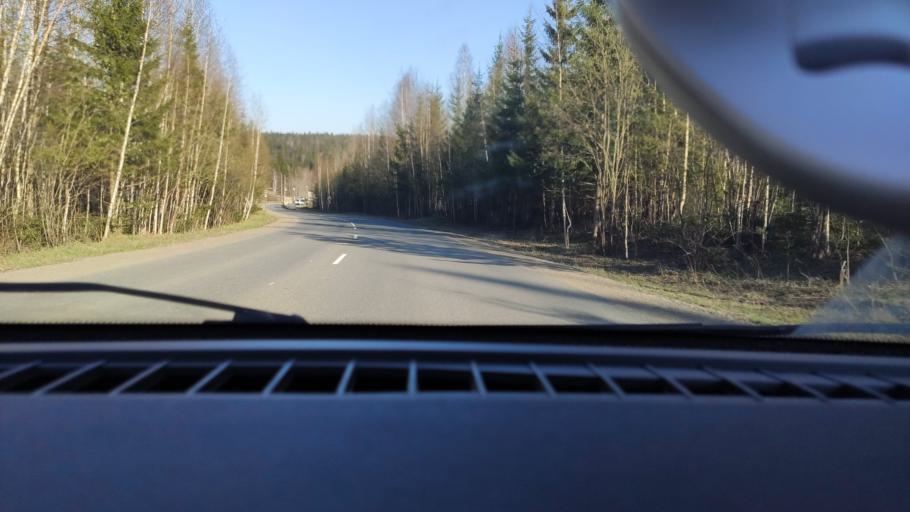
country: RU
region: Perm
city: Polazna
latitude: 58.1227
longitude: 56.4442
